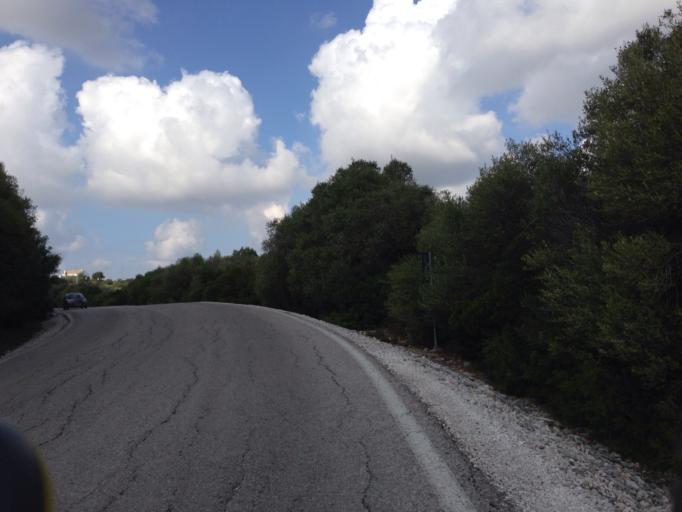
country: ES
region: Andalusia
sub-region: Provincia de Cadiz
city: Conil de la Frontera
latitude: 36.3424
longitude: -6.0245
